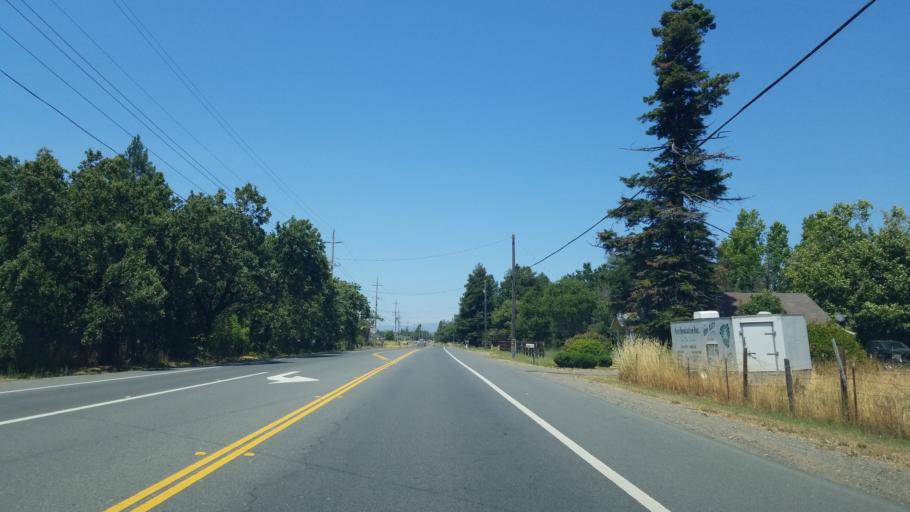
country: US
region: California
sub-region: Sonoma County
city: Roseland
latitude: 38.3775
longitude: -122.7414
